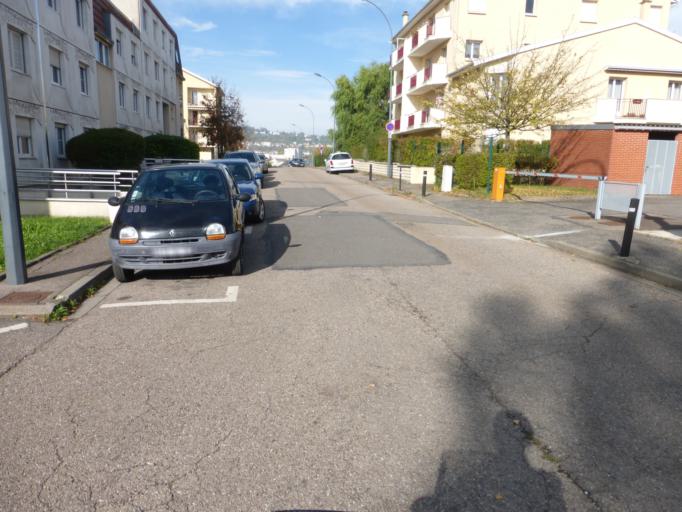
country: FR
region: Lorraine
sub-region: Departement de Meurthe-et-Moselle
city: Villers-les-Nancy
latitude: 48.6738
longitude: 6.1572
